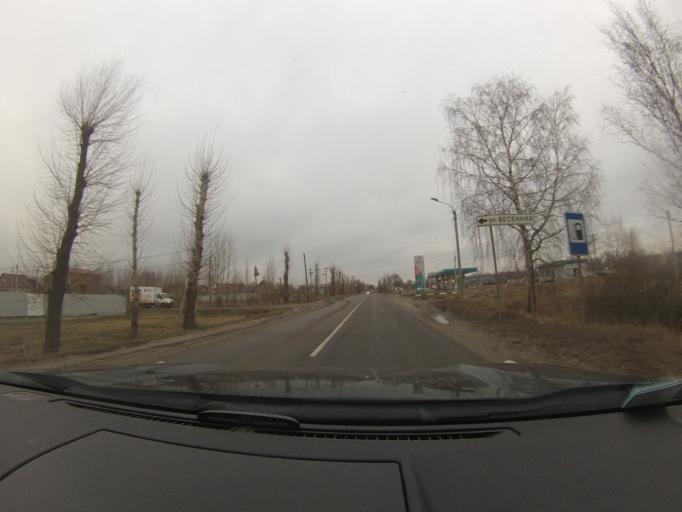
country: RU
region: Moskovskaya
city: Lopatinskiy
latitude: 55.3331
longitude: 38.7260
